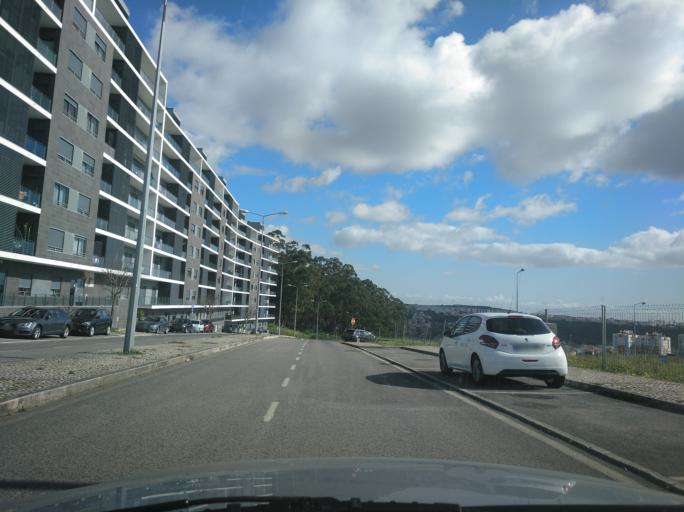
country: PT
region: Lisbon
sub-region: Odivelas
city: Povoa de Santo Adriao
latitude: 38.8100
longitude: -9.1686
